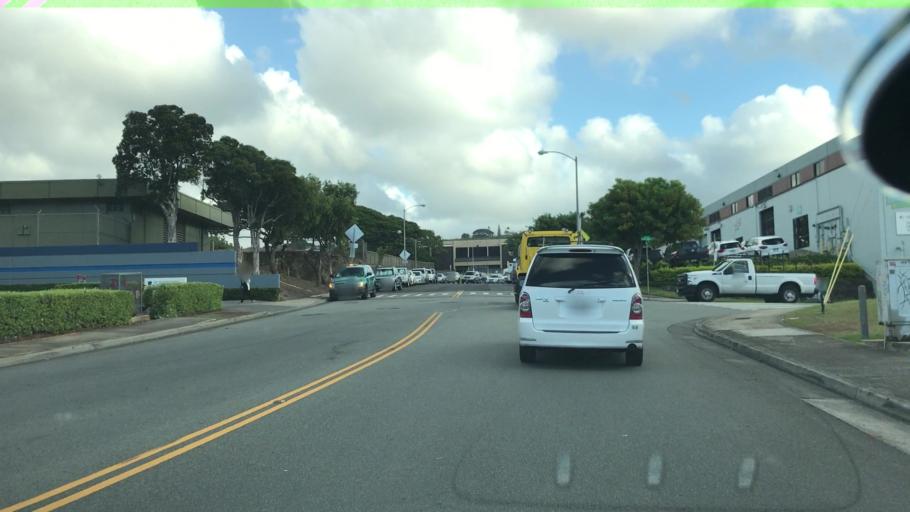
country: US
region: Hawaii
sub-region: Honolulu County
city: Halawa Heights
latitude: 21.3718
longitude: -157.9150
